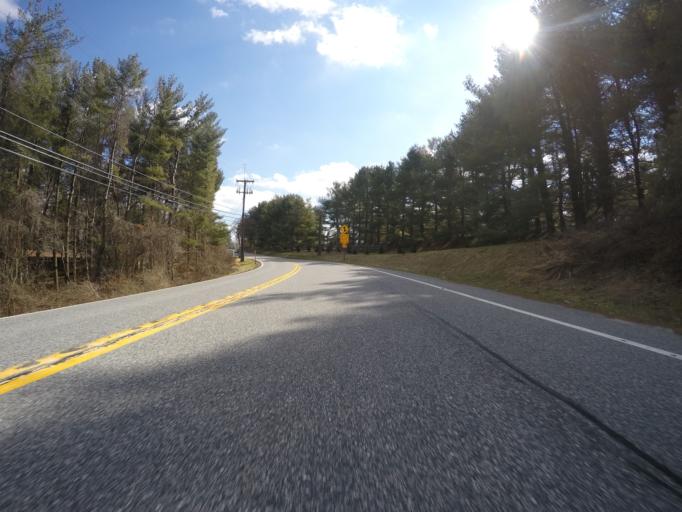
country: US
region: Maryland
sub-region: Baltimore County
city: Mays Chapel
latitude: 39.4555
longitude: -76.6910
